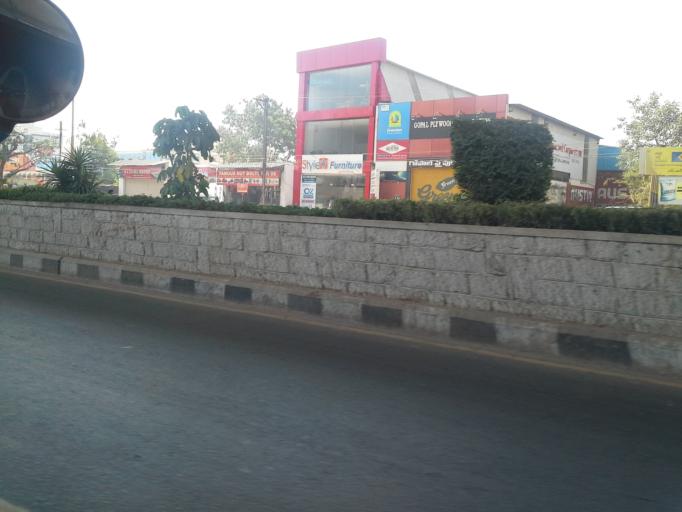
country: IN
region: Telangana
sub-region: Hyderabad
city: Hyderabad
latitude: 17.3709
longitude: 78.4294
